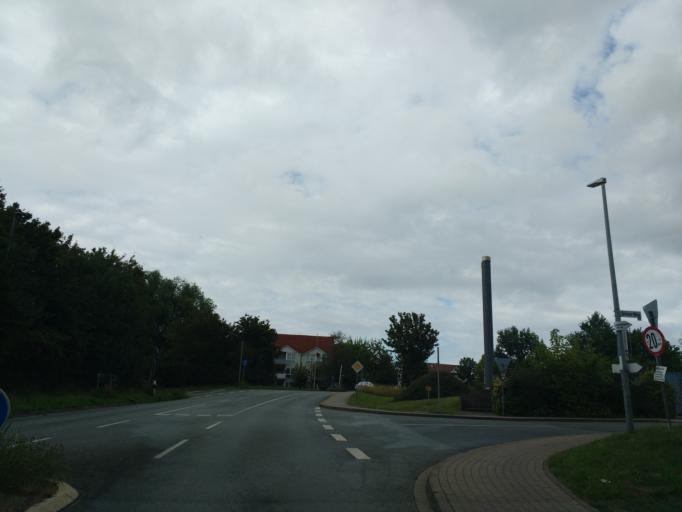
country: DE
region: Lower Saxony
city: Bad Laer
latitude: 52.0988
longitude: 8.0972
